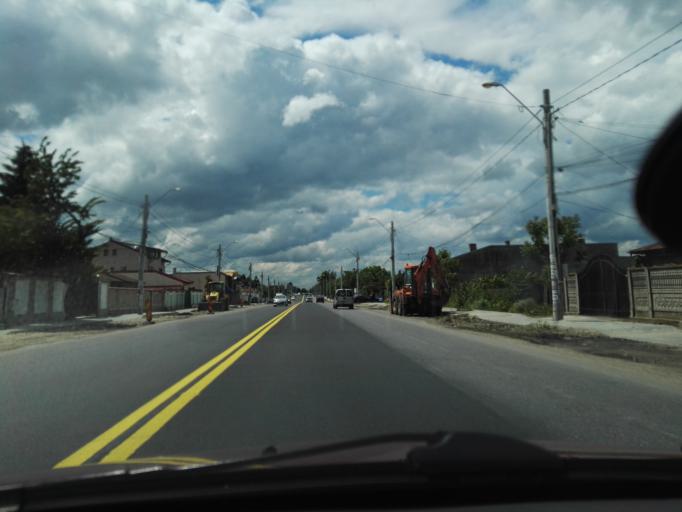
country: RO
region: Ilfov
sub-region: Comuna Jilava
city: Jilava
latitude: 44.3373
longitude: 26.0800
